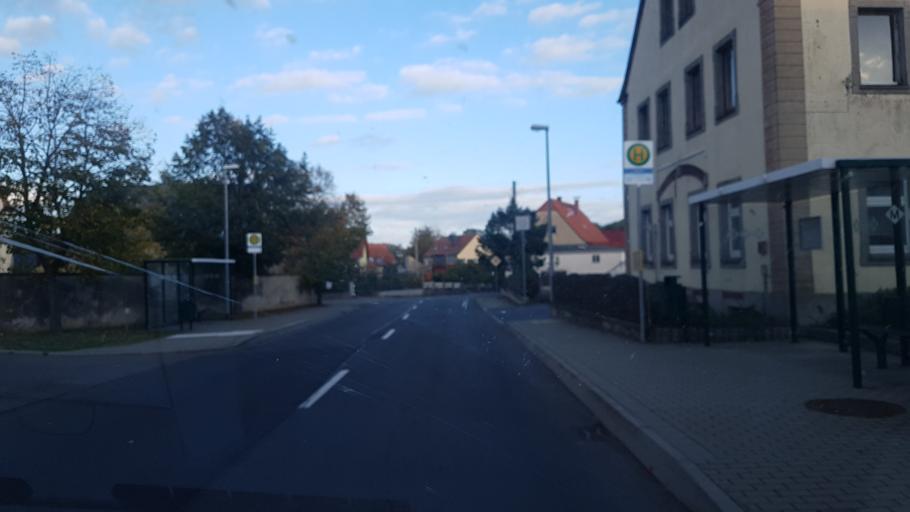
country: DE
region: Saxony
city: Dahlen
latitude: 51.3377
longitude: 13.0314
